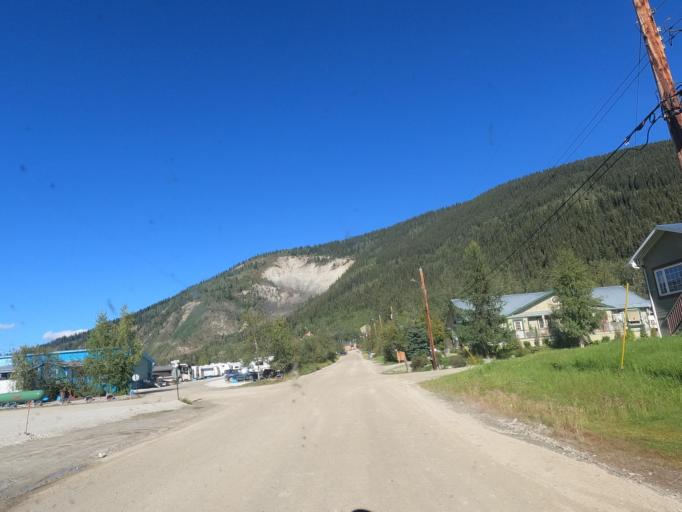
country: CA
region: Yukon
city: Dawson City
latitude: 64.0625
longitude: -139.4271
